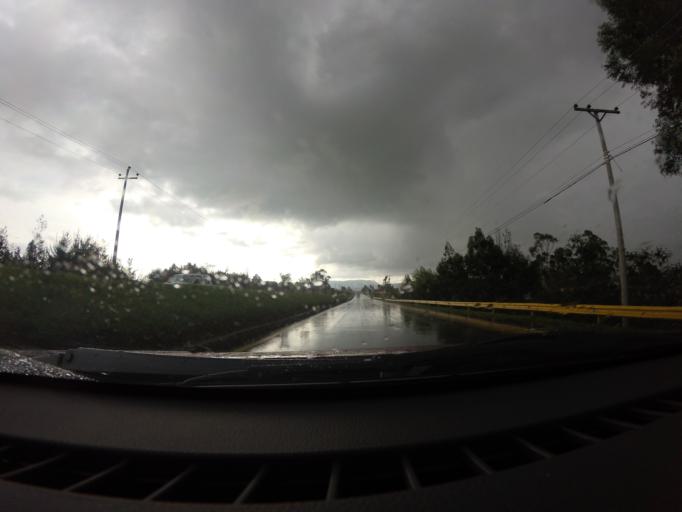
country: CO
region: Cundinamarca
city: El Rosal
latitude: 4.8245
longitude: -74.2364
